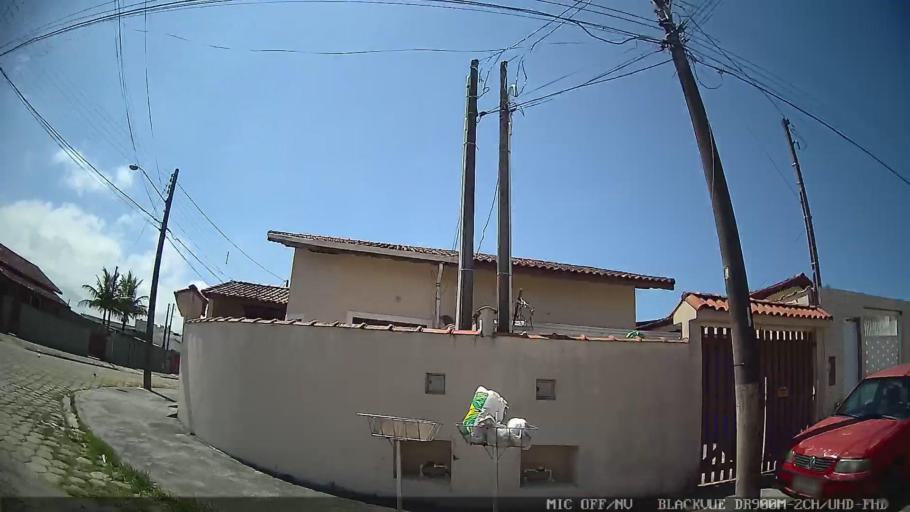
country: BR
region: Sao Paulo
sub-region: Peruibe
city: Peruibe
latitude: -24.3018
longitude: -46.9912
